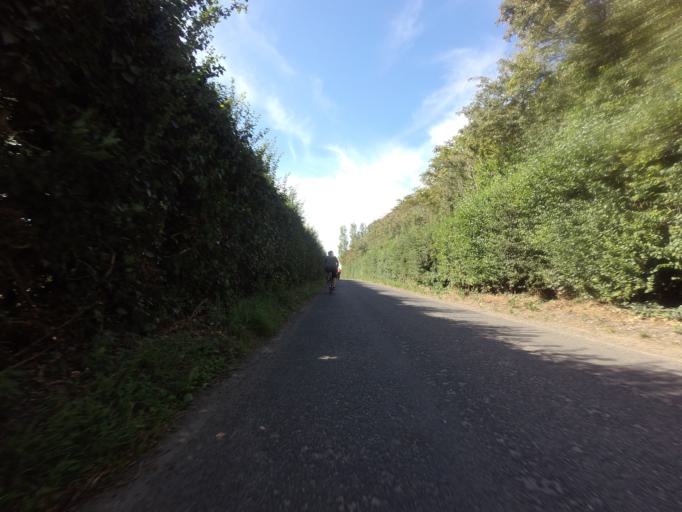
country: GB
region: England
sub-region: Kent
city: Birchington-on-Sea
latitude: 51.3454
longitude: 1.2621
